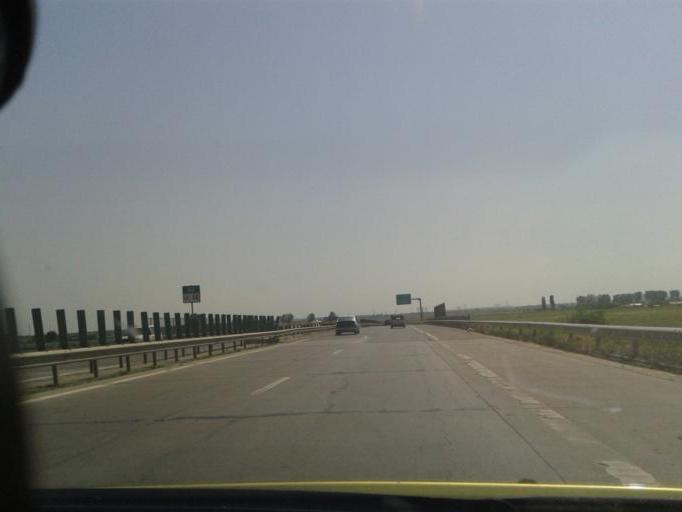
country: RO
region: Ilfov
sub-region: Comuna Cernica
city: Caldararu
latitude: 44.4087
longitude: 26.2592
